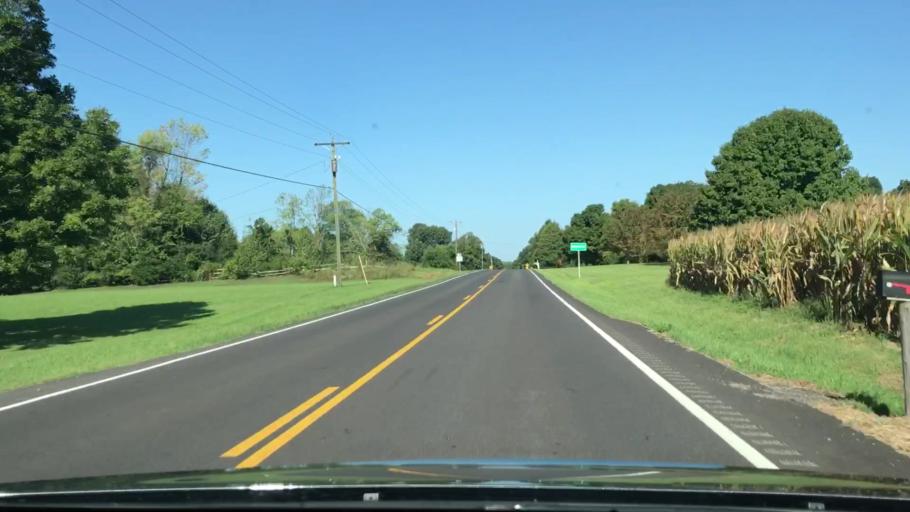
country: US
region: Kentucky
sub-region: Marshall County
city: Benton
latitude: 36.7675
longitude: -88.4323
